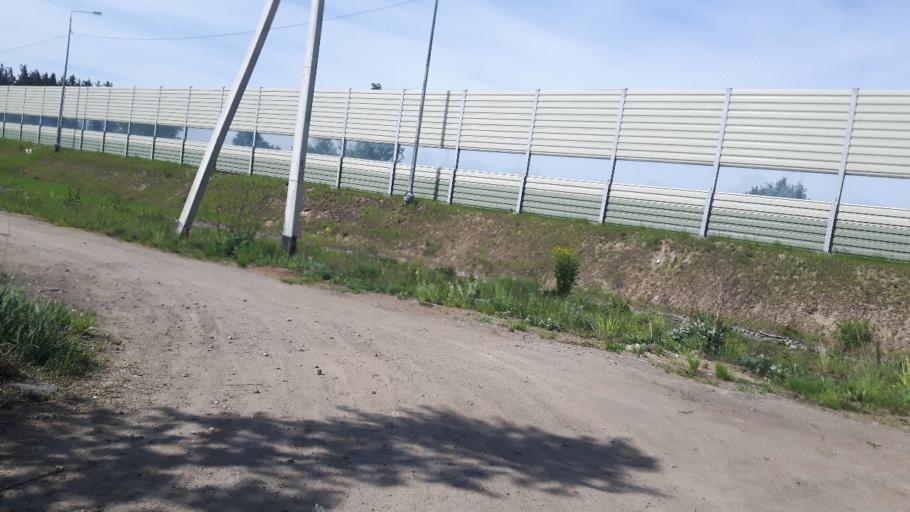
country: RU
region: Leningrad
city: Vistino
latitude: 59.6757
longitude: 28.4374
